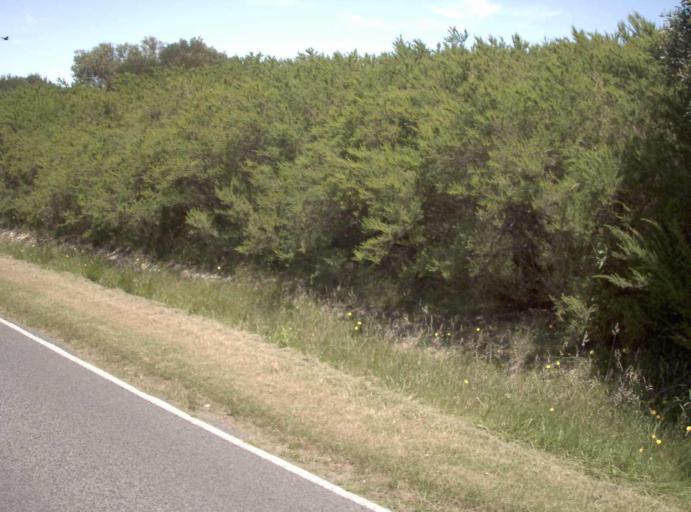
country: AU
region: Victoria
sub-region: Bass Coast
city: North Wonthaggi
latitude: -38.7743
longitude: 146.1611
